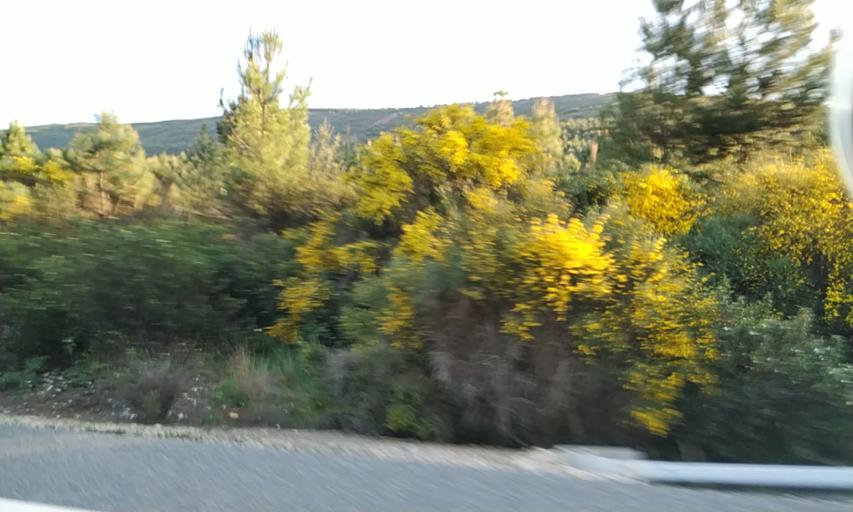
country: PT
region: Portalegre
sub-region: Portalegre
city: Sao Juliao
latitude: 39.3459
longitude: -7.2982
